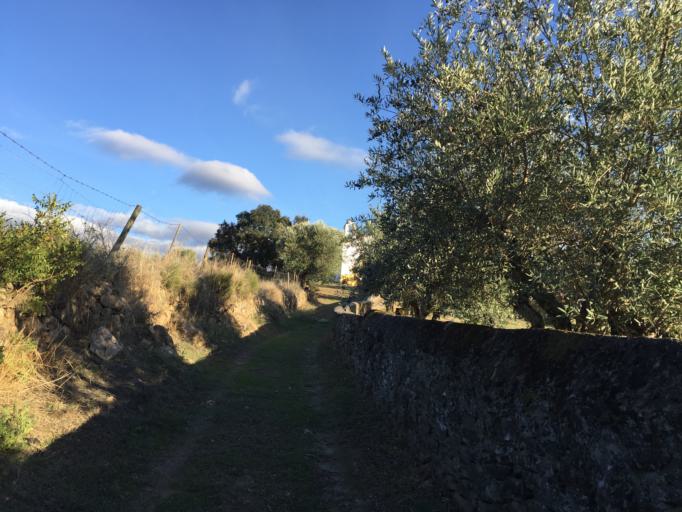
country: PT
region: Portalegre
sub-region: Alter do Chao
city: Alter do Chao
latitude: 39.2835
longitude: -7.6401
